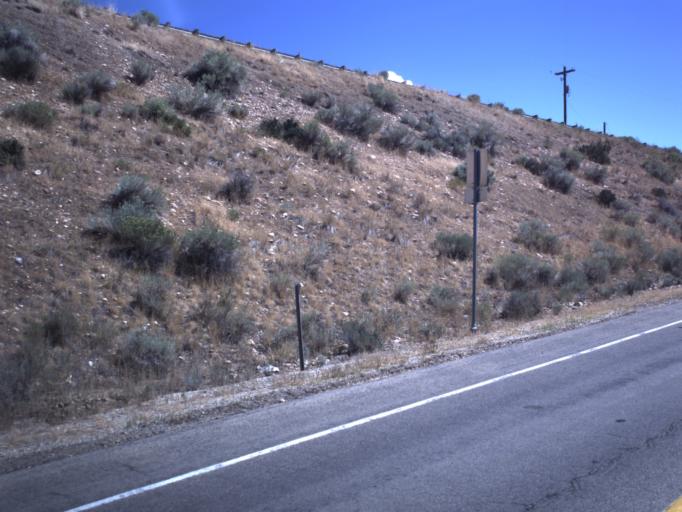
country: US
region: Utah
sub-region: Summit County
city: Francis
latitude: 40.6107
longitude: -111.2885
